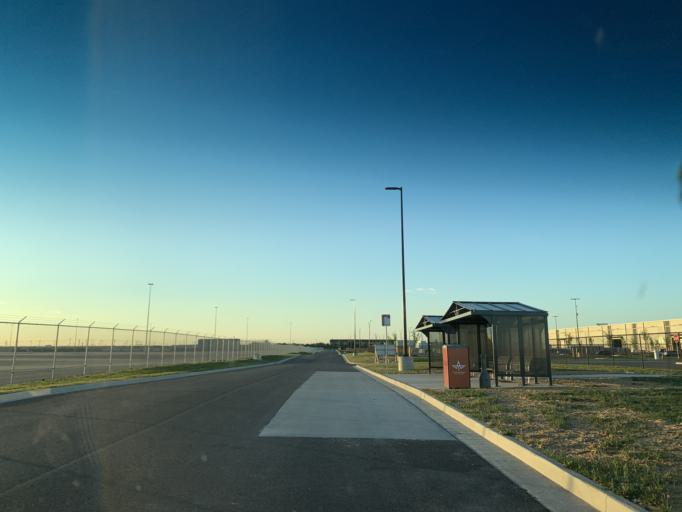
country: US
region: Maryland
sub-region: Baltimore County
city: Edgemere
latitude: 39.2195
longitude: -76.4852
